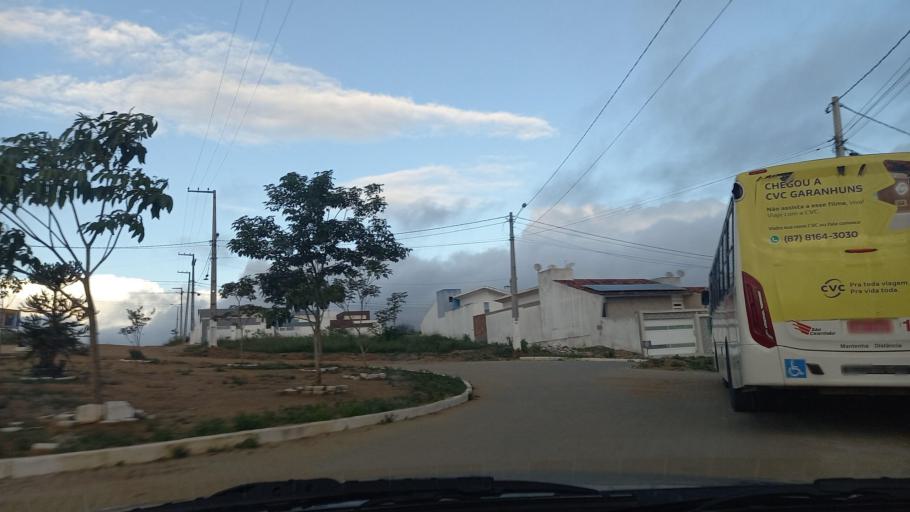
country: BR
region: Pernambuco
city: Garanhuns
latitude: -8.8923
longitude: -36.4388
